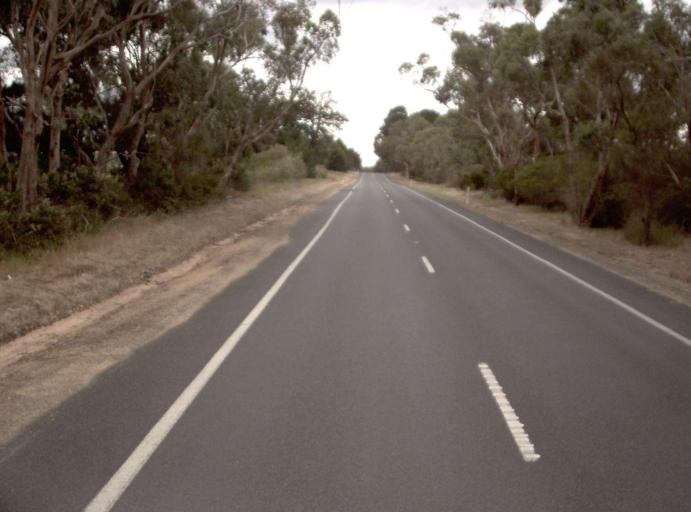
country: AU
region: Victoria
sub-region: Wellington
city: Sale
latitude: -38.2025
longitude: 147.0743
